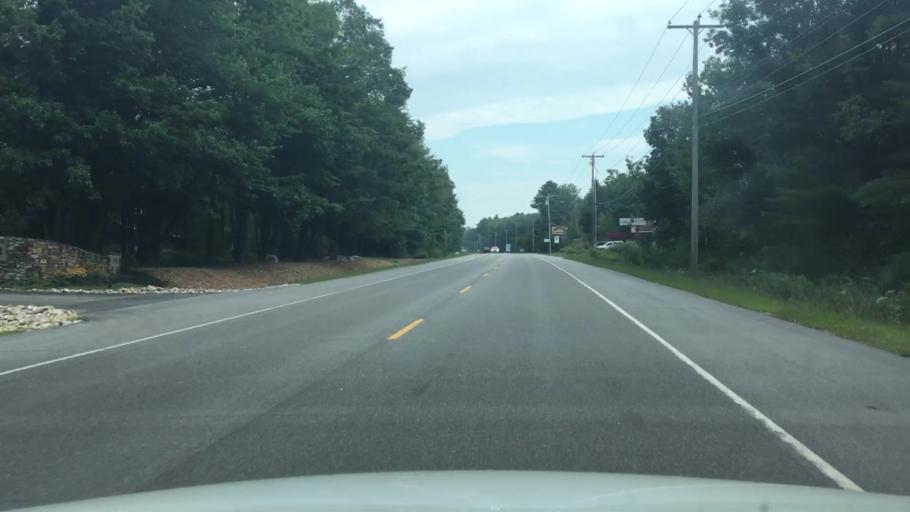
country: US
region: Maine
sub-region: Cumberland County
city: Falmouth Foreside
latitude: 43.7410
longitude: -70.2195
